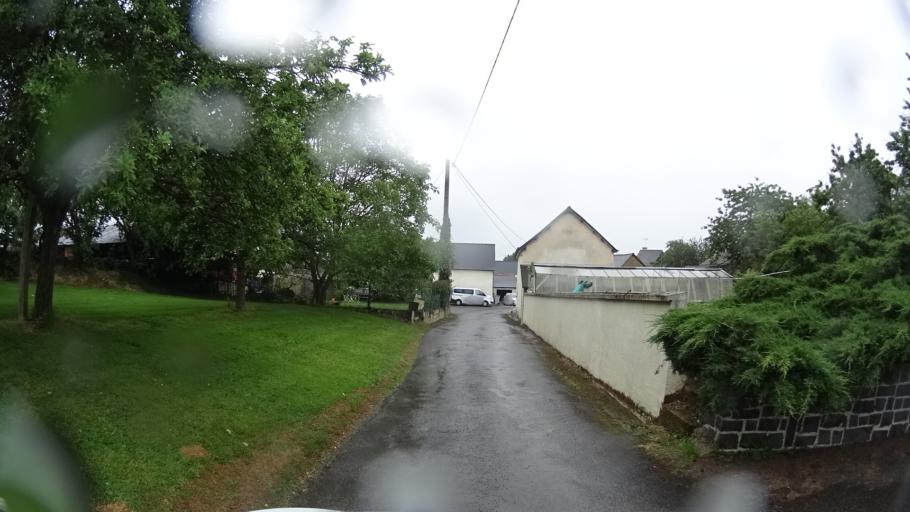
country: FR
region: Brittany
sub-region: Departement d'Ille-et-Vilaine
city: Saint-Erblon
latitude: 48.0253
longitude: -1.6403
